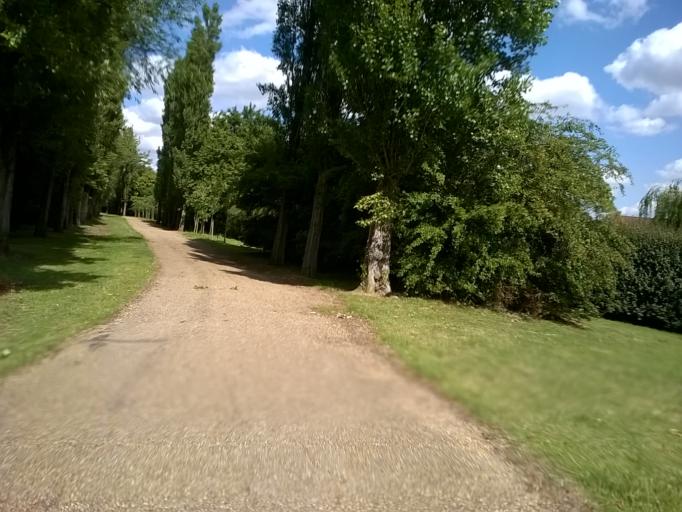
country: GB
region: England
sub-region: Milton Keynes
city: Milton Keynes
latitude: 52.0616
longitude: -0.7387
